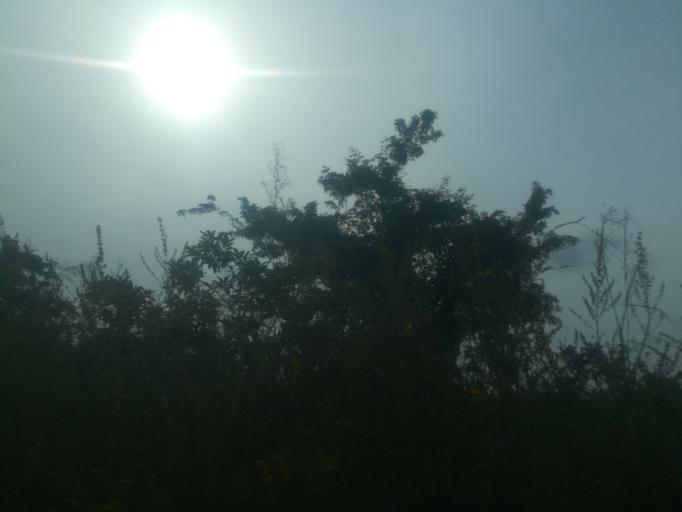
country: NG
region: Ogun
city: Ayetoro
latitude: 7.3210
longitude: 3.0683
